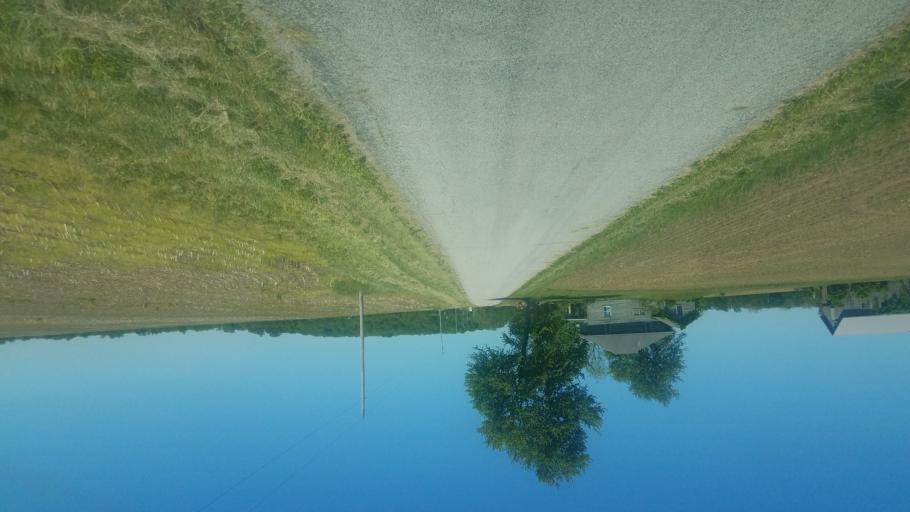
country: US
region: Ohio
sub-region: Champaign County
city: Saint Paris
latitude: 40.2004
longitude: -84.0164
